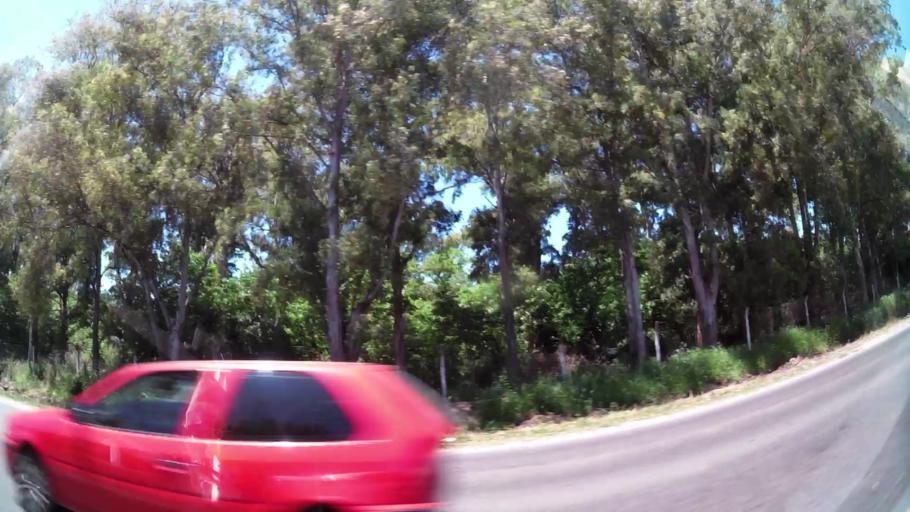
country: AR
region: Buenos Aires
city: Hurlingham
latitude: -34.5177
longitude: -58.6705
